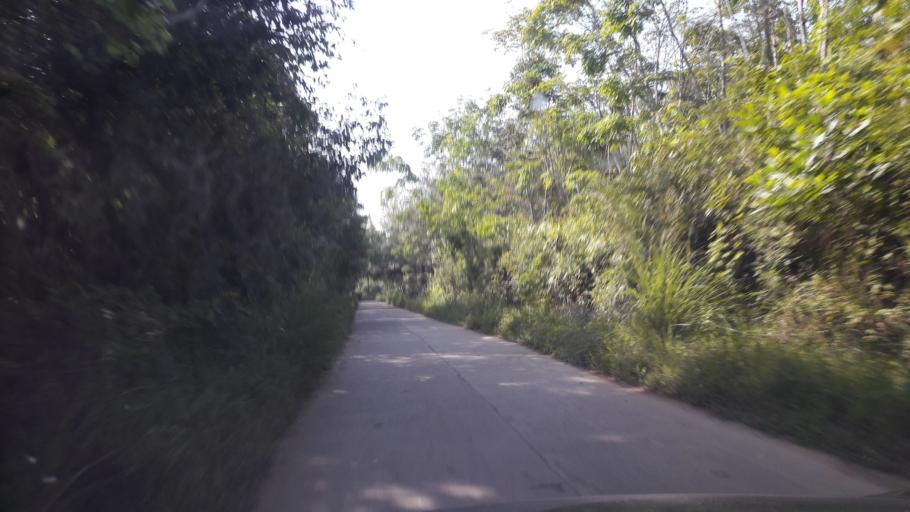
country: ID
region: South Sumatra
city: Gunungmenang
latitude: -3.3142
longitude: 103.9678
